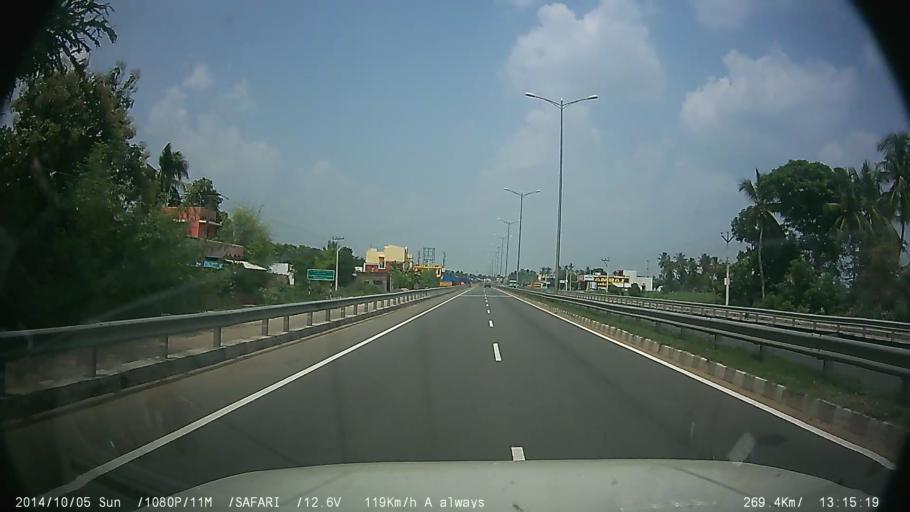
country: IN
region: Tamil Nadu
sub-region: Villupuram
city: Villupuram
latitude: 11.9914
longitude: 79.5126
